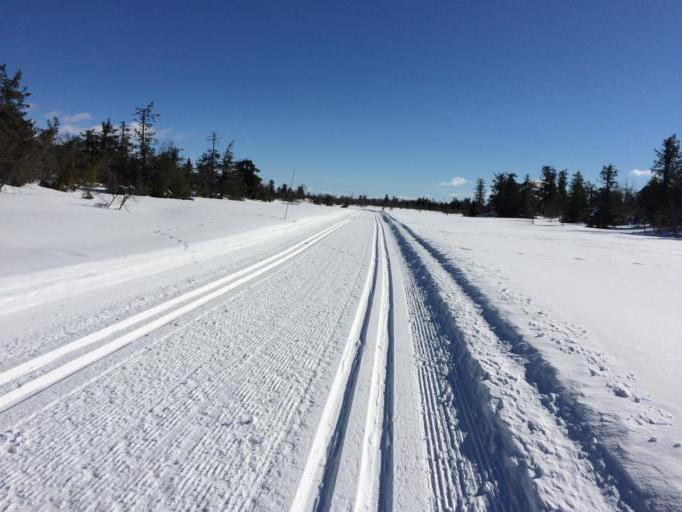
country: NO
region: Oppland
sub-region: Gausdal
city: Segalstad bru
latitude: 61.3088
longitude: 10.0971
